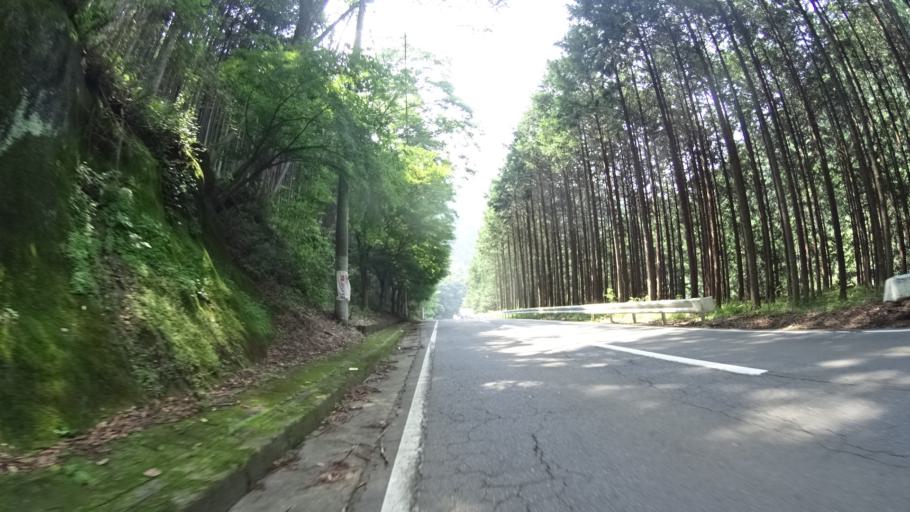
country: JP
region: Gunma
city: Tomioka
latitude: 36.0868
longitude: 138.8020
